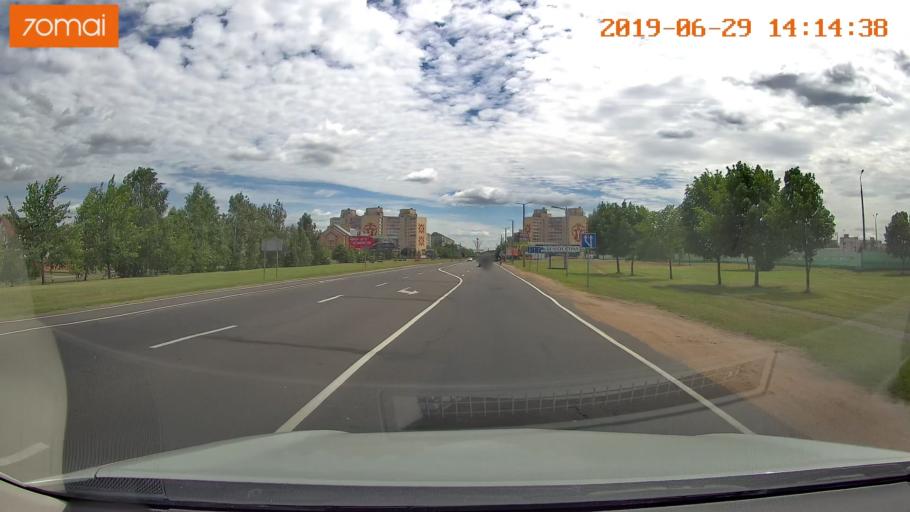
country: BY
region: Minsk
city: Salihorsk
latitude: 52.7944
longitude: 27.5172
